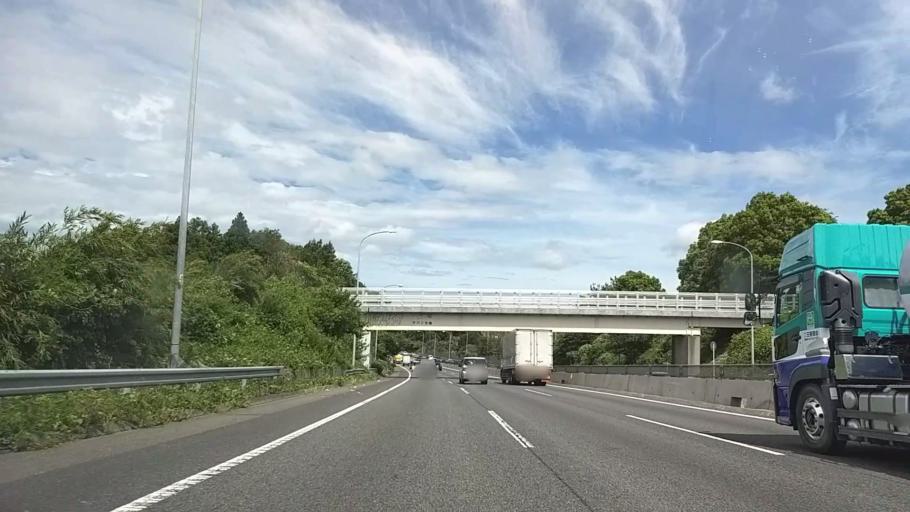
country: JP
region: Kanagawa
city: Minami-rinkan
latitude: 35.4735
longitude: 139.5303
